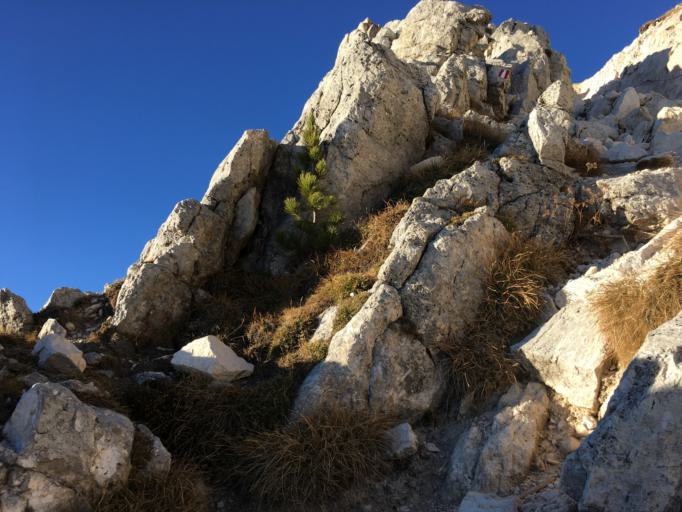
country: IT
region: Trentino-Alto Adige
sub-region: Provincia di Trento
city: Varena
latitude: 46.3539
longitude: 11.4443
